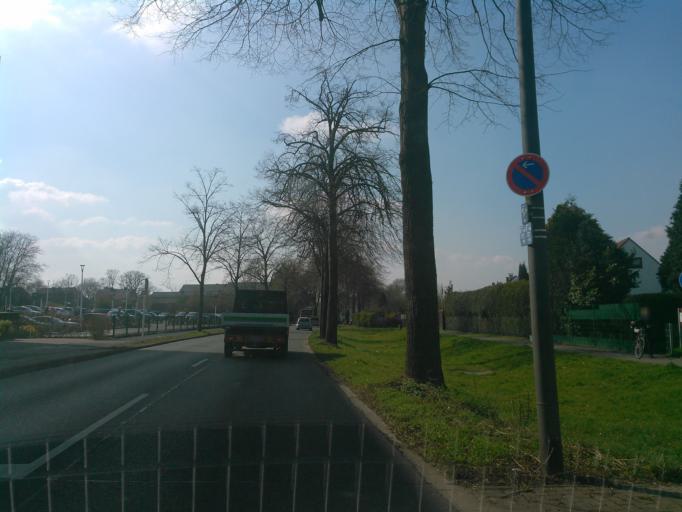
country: DE
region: North Rhine-Westphalia
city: Marl
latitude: 51.6532
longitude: 7.0851
